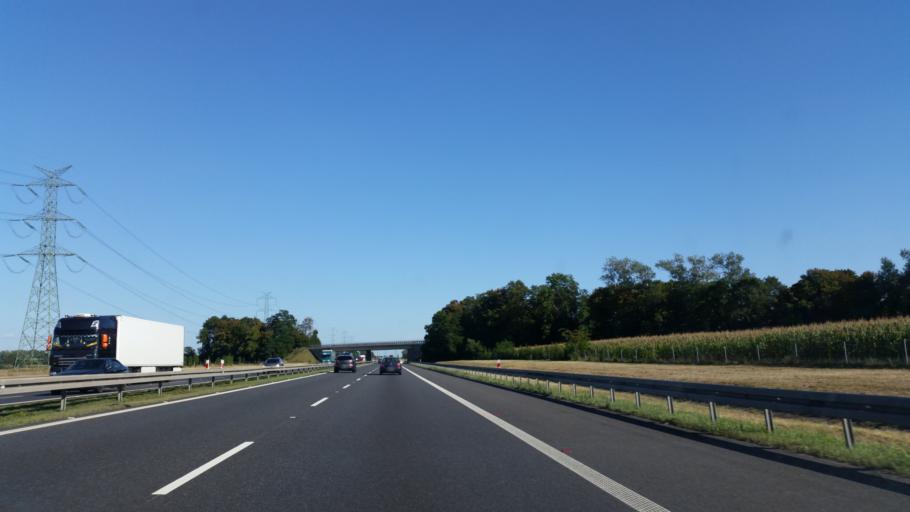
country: PL
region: Lower Silesian Voivodeship
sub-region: Powiat olawski
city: Wierzbno
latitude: 50.9113
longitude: 17.1507
